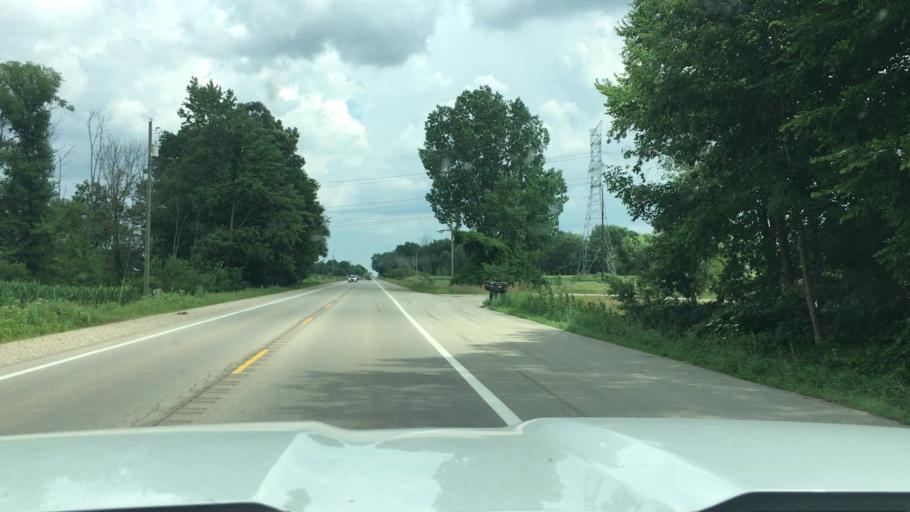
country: US
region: Michigan
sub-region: Kent County
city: Cedar Springs
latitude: 43.1762
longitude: -85.4395
